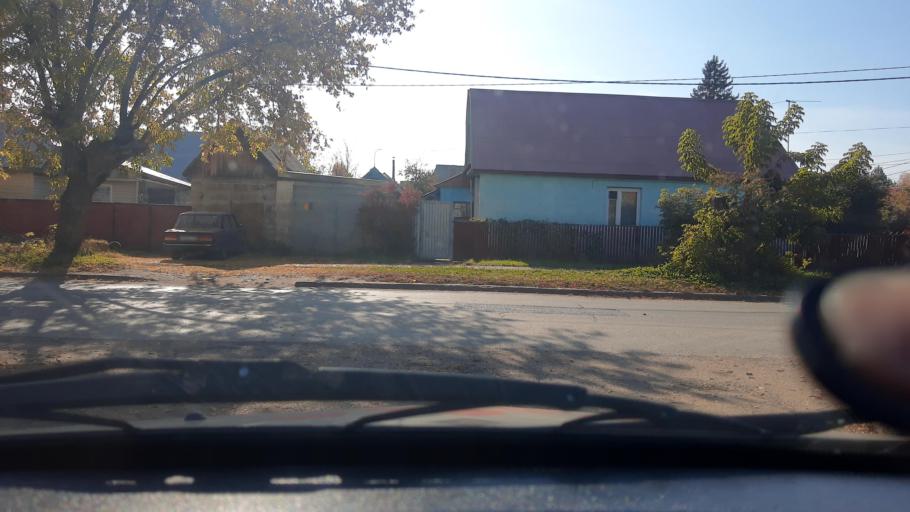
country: RU
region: Bashkortostan
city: Ufa
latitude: 54.7987
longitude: 56.1453
